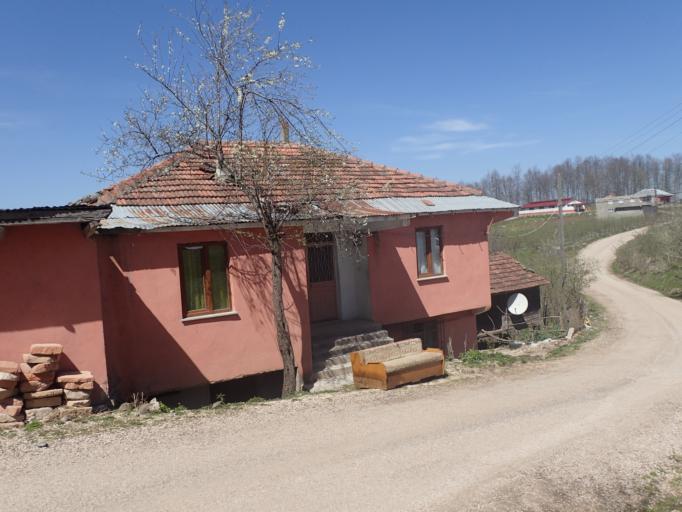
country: TR
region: Ordu
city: Aybasti
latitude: 40.7034
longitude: 37.2726
